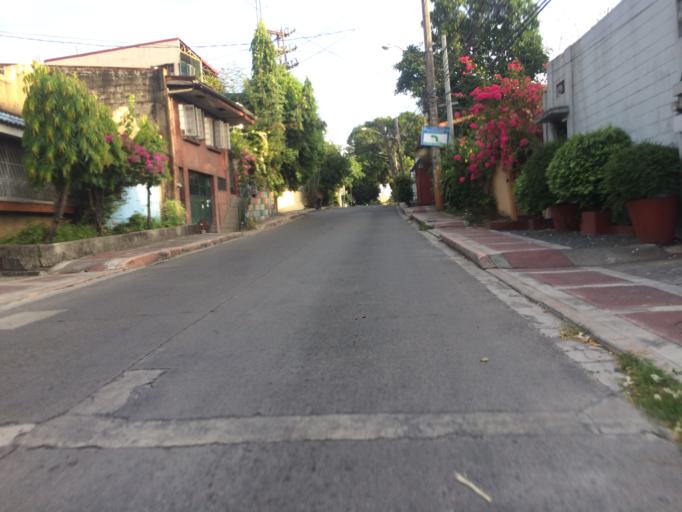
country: PH
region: Calabarzon
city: Bagong Pagasa
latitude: 14.6726
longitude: 121.0231
